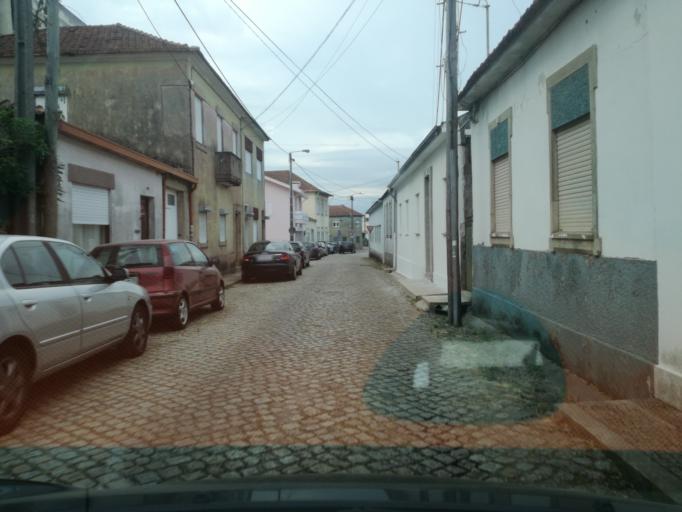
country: PT
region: Porto
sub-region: Maia
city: Maia
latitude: 41.2340
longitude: -8.6089
